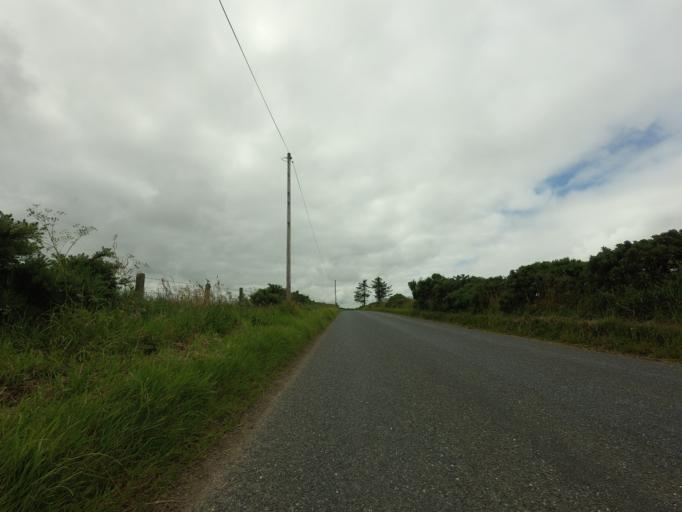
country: GB
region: Scotland
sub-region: Aberdeenshire
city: Rosehearty
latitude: 57.5415
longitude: -2.2052
